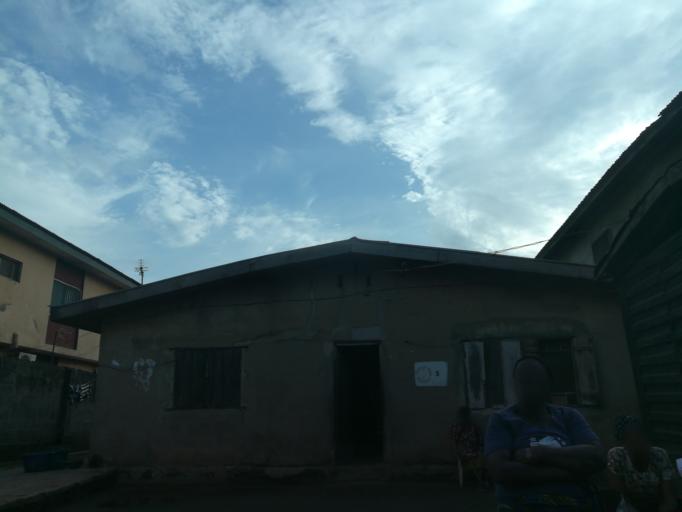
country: NG
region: Lagos
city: Ebute Ikorodu
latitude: 6.6147
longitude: 3.4742
